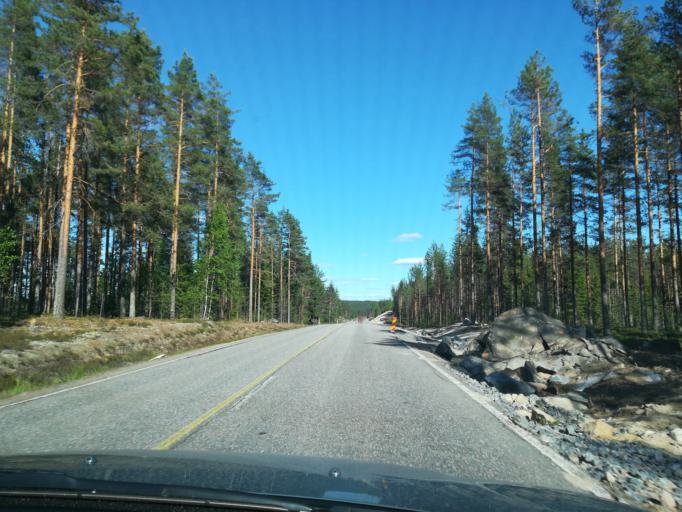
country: FI
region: Southern Savonia
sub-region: Mikkeli
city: Puumala
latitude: 61.4653
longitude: 28.3671
